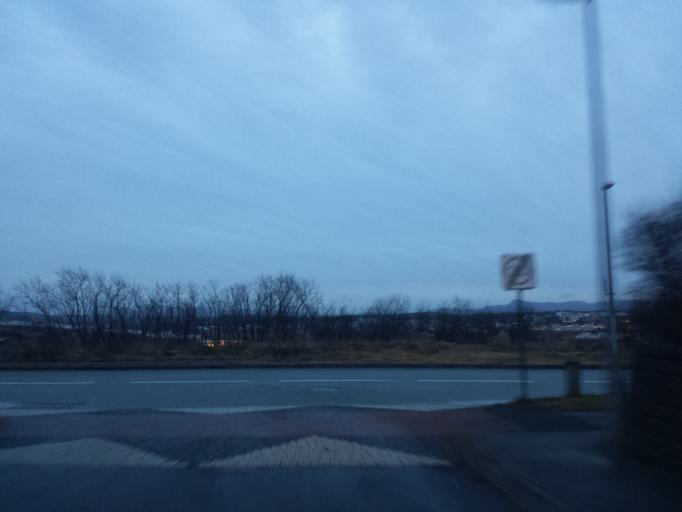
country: IS
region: Capital Region
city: Mosfellsbaer
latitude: 64.1361
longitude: -21.7723
